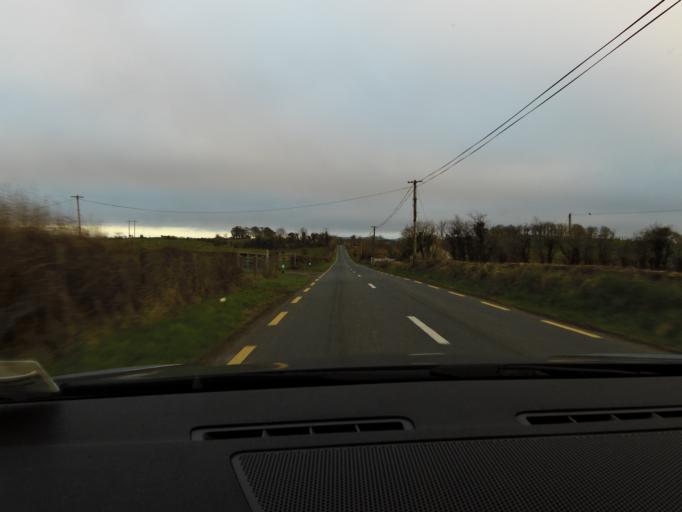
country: IE
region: Connaught
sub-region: Sligo
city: Ballymote
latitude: 54.0144
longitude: -8.5546
